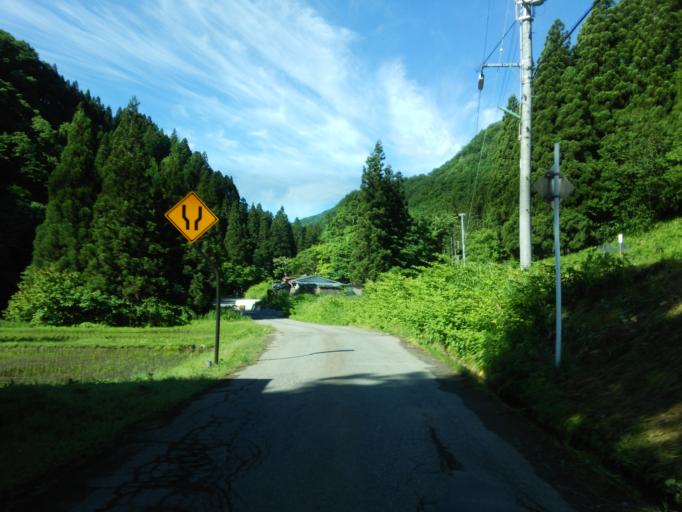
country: JP
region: Fukushima
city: Kitakata
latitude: 37.3852
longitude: 139.8137
